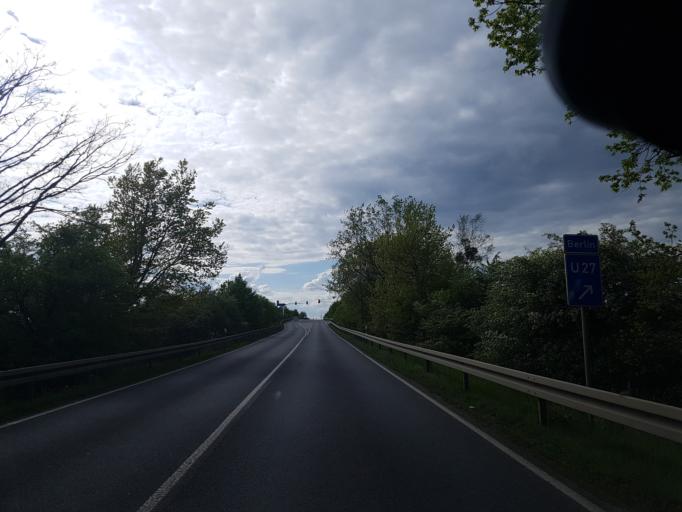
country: DE
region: Brandenburg
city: Grossraschen
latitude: 51.5871
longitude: 13.9456
